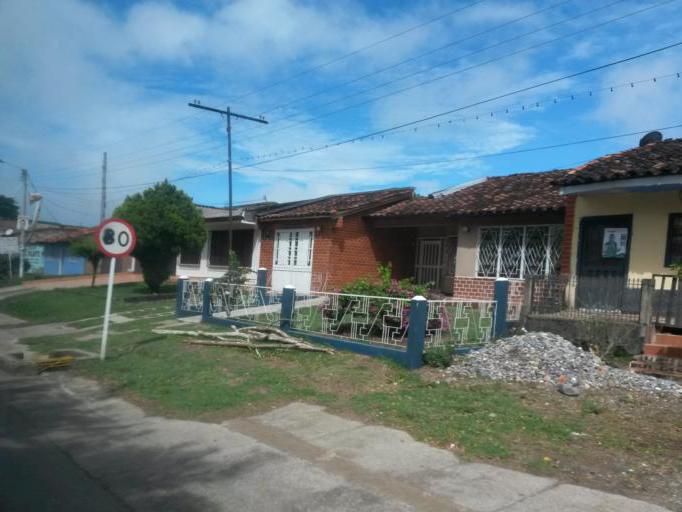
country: CO
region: Cauca
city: El Bordo
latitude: 2.1245
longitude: -76.9774
